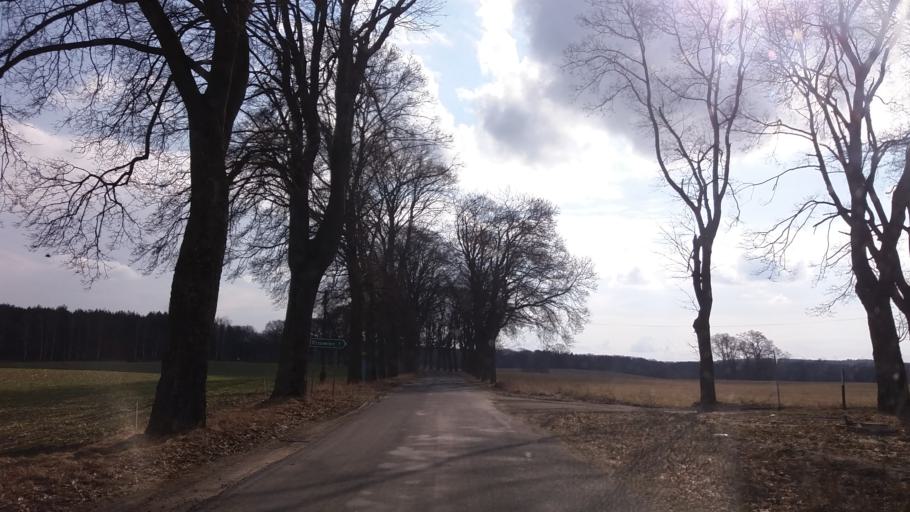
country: PL
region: West Pomeranian Voivodeship
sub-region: Powiat choszczenski
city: Recz
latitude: 53.1636
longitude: 15.6150
